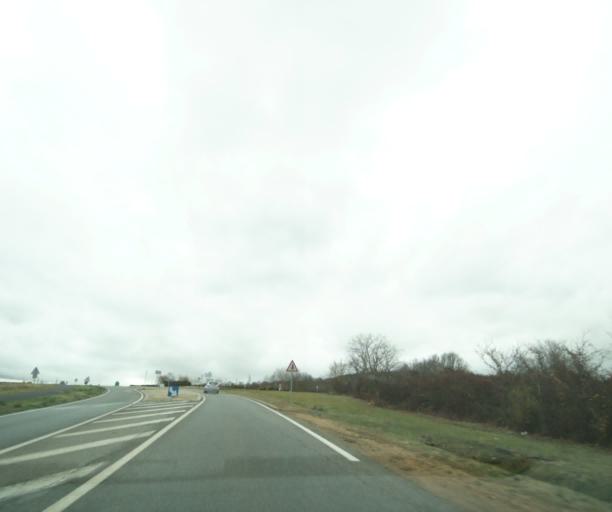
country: FR
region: Auvergne
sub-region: Departement du Puy-de-Dome
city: Cournon-d'Auvergne
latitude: 45.7636
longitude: 3.2064
